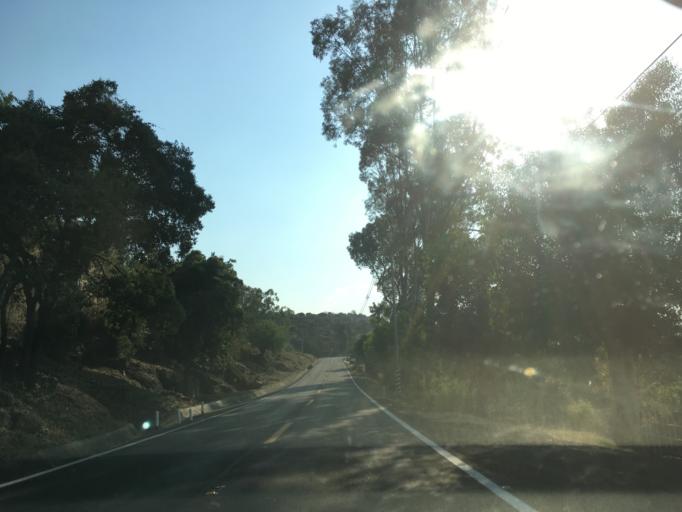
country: MX
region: Michoacan
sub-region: Zinapecuaro
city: Santa Clara del Tule
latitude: 19.8057
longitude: -100.8656
